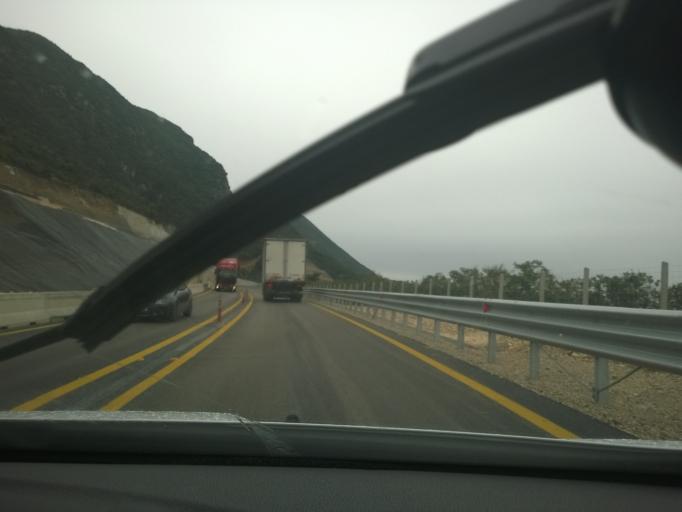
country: GR
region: West Greece
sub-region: Nomos Achaias
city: Kamarai
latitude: 38.3242
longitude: 21.9107
